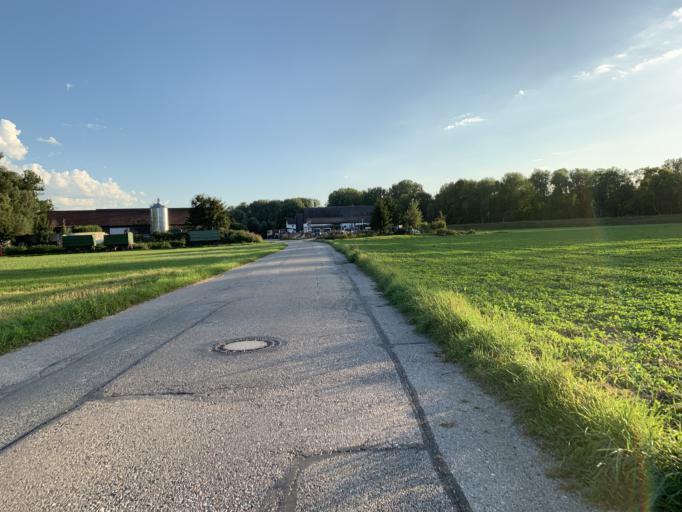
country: DE
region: Bavaria
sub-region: Upper Bavaria
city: Freising
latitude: 48.3829
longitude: 11.7475
